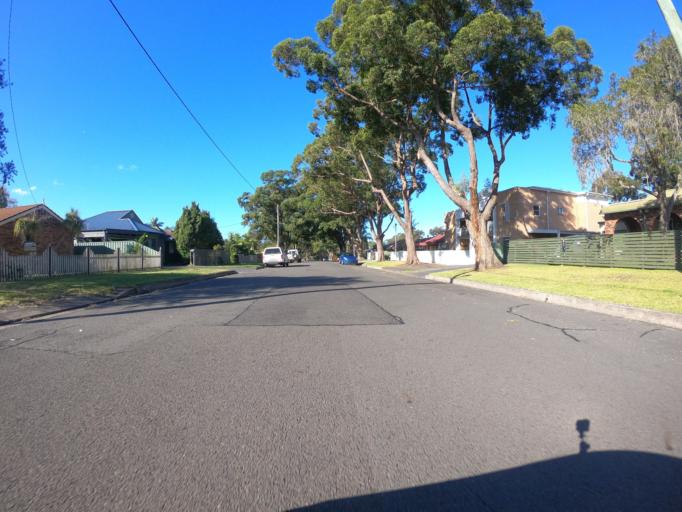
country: AU
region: New South Wales
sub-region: Wollongong
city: East Corrimal
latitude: -34.3610
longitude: 150.9044
